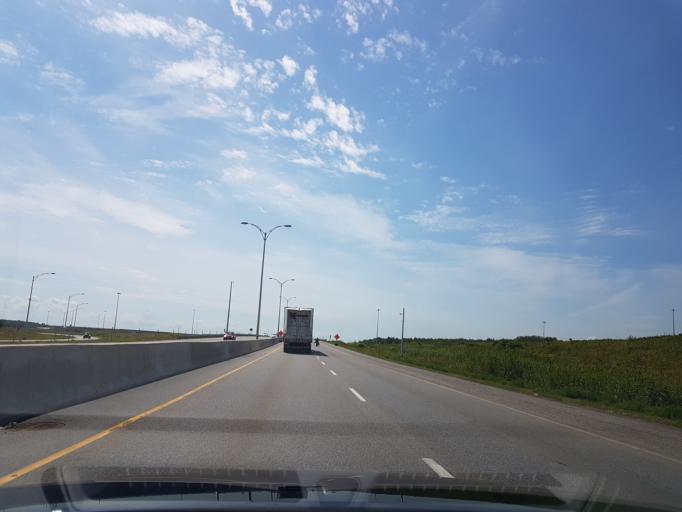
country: CA
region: Quebec
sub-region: Monteregie
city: Vaudreuil-Dorion
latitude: 45.3621
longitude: -74.0441
